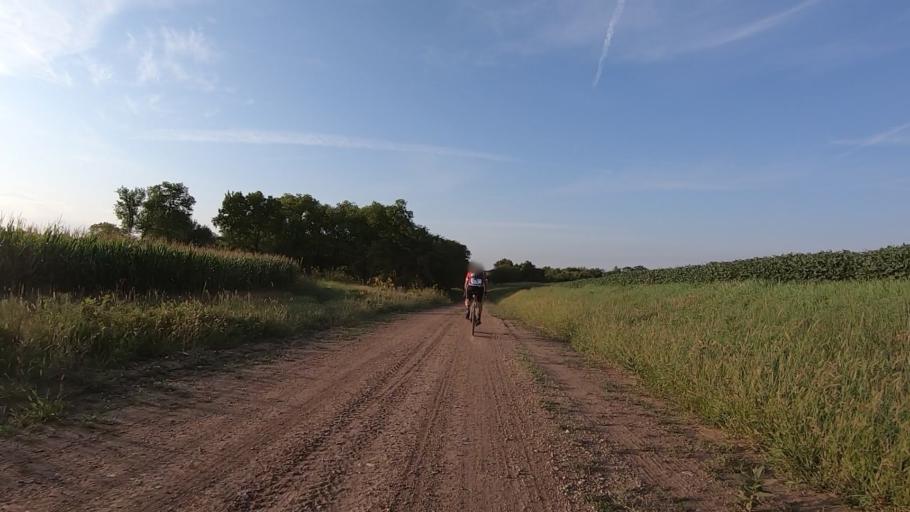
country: US
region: Kansas
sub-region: Marshall County
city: Blue Rapids
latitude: 39.7625
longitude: -96.7508
